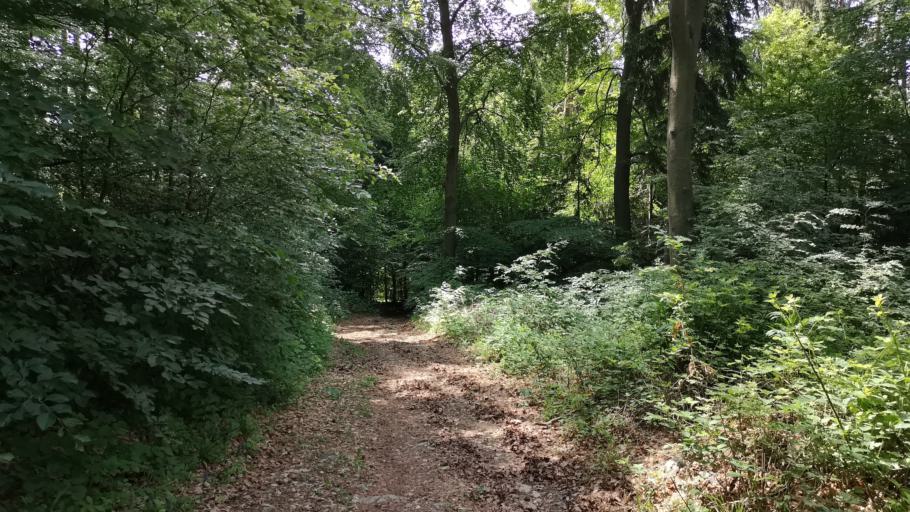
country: AT
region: Styria
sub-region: Graz Stadt
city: Wetzelsdorf
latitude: 47.0360
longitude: 15.3720
